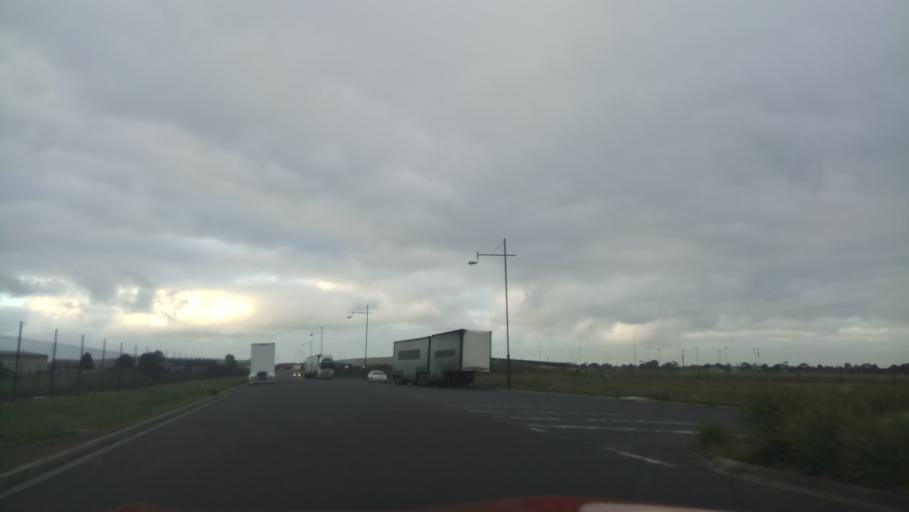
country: AU
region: Victoria
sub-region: Hobsons Bay
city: Laverton
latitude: -37.8522
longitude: 144.7891
